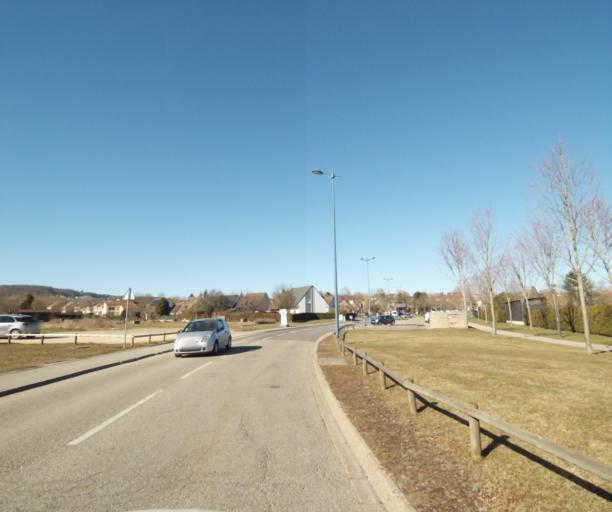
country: FR
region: Lorraine
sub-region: Departement de Meurthe-et-Moselle
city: Vandoeuvre-les-Nancy
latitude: 48.6483
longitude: 6.1953
